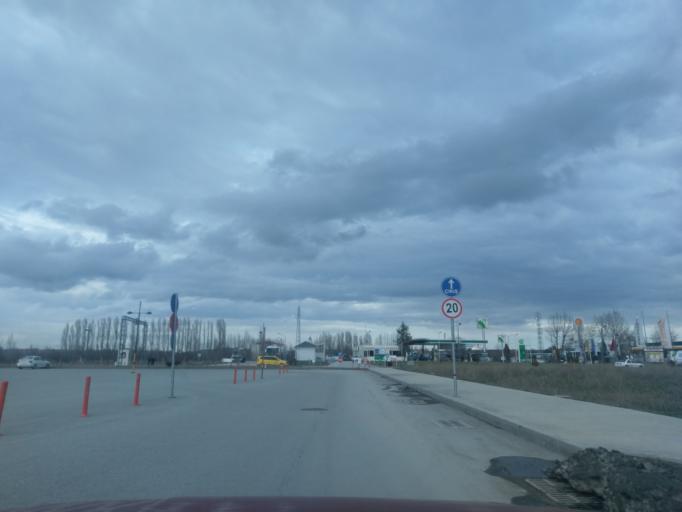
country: TR
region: Kuetahya
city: Kutahya
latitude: 39.4356
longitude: 29.9971
